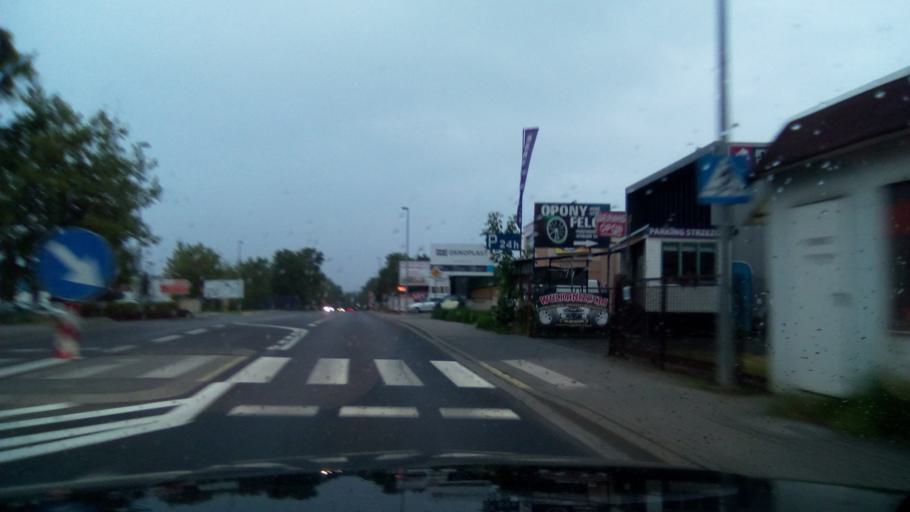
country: PL
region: Greater Poland Voivodeship
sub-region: Powiat poznanski
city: Swarzedz
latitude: 52.4187
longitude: 17.0845
